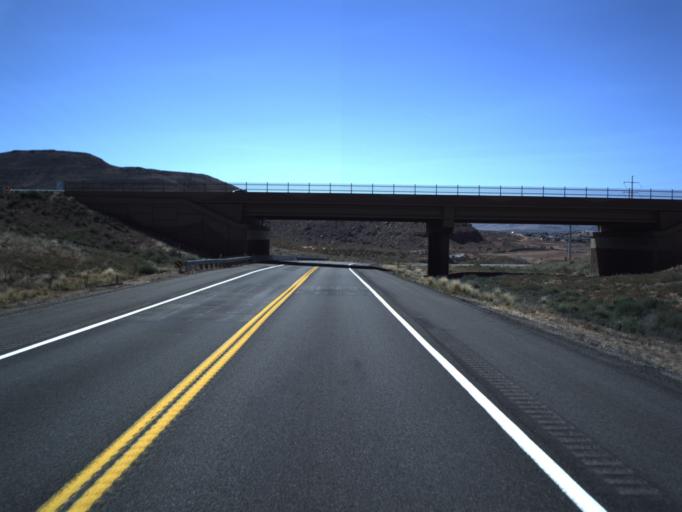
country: US
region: Utah
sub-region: Washington County
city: Washington
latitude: 37.0157
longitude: -113.4940
